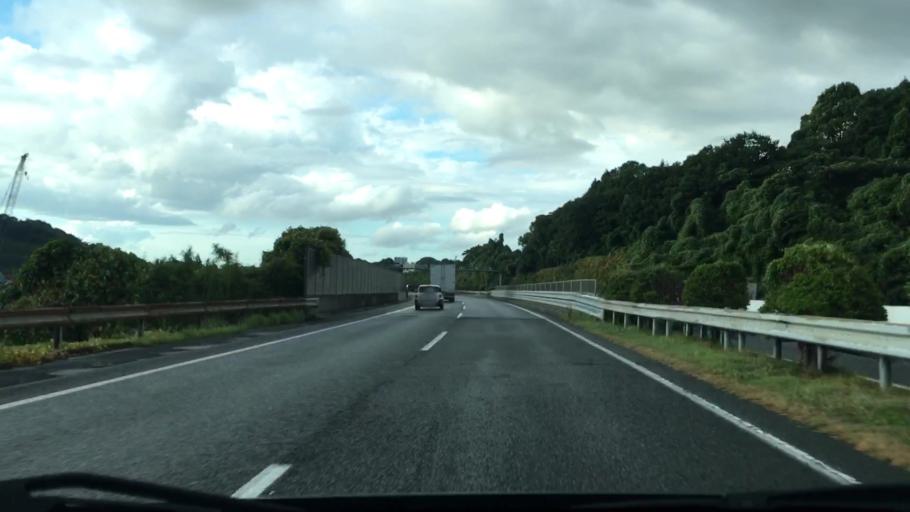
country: JP
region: Fukuoka
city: Koga
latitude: 33.6963
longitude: 130.4852
